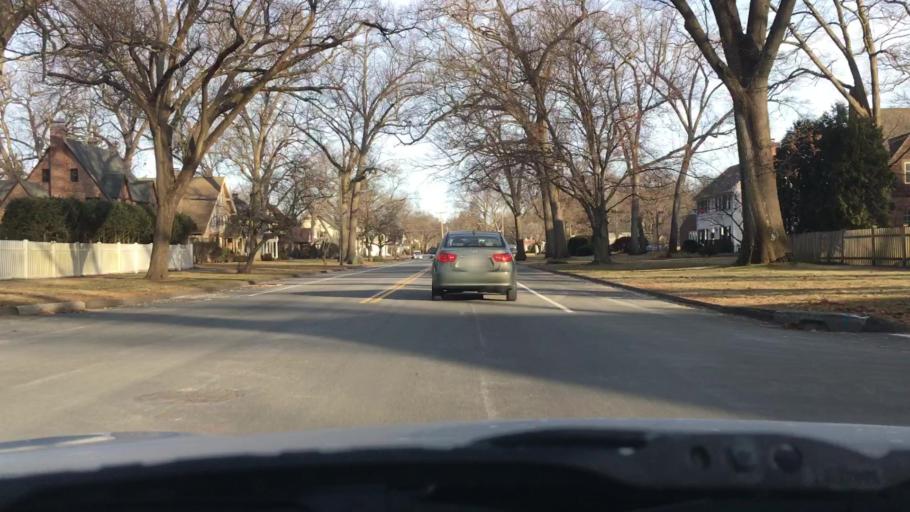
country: US
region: Massachusetts
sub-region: Hampden County
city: Longmeadow
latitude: 42.0631
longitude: -72.5734
